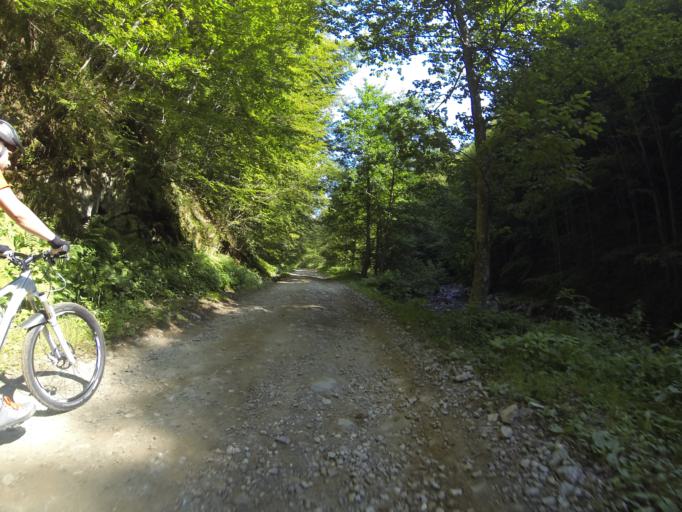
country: RO
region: Valcea
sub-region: Comuna Costesti
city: Bistrita
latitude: 45.2298
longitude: 24.0029
